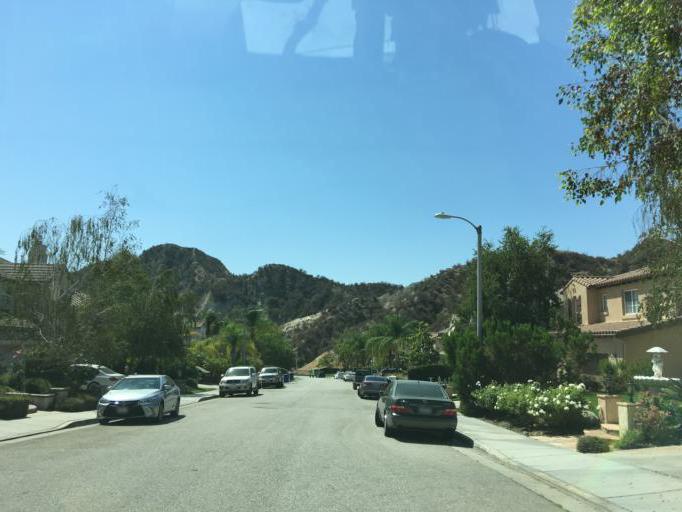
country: US
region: California
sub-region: Los Angeles County
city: Valencia
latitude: 34.3862
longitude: -118.6013
